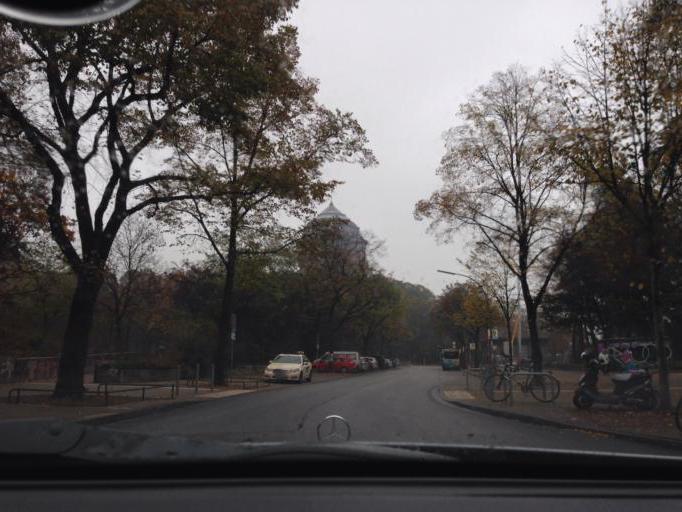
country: DE
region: Hamburg
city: St. Pauli
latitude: 53.5642
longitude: 9.9666
